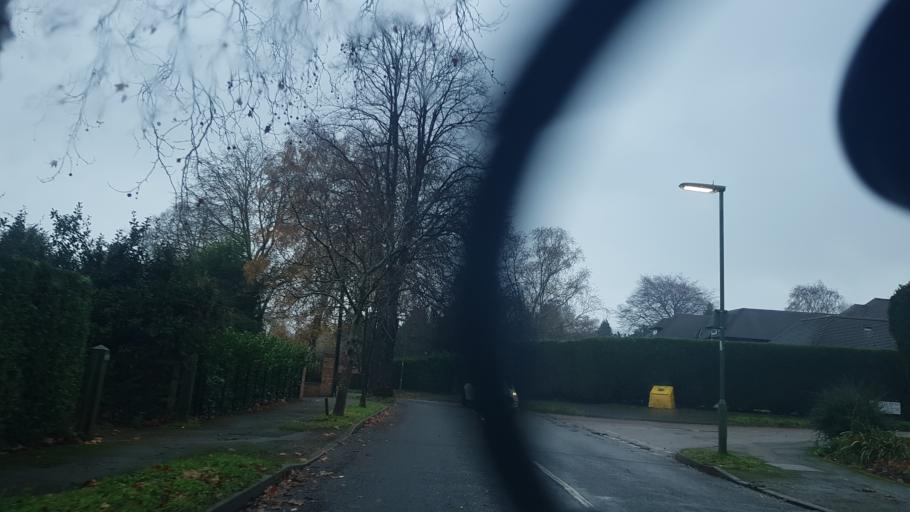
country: GB
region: England
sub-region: Surrey
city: Great Bookham
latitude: 51.2821
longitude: -0.3621
